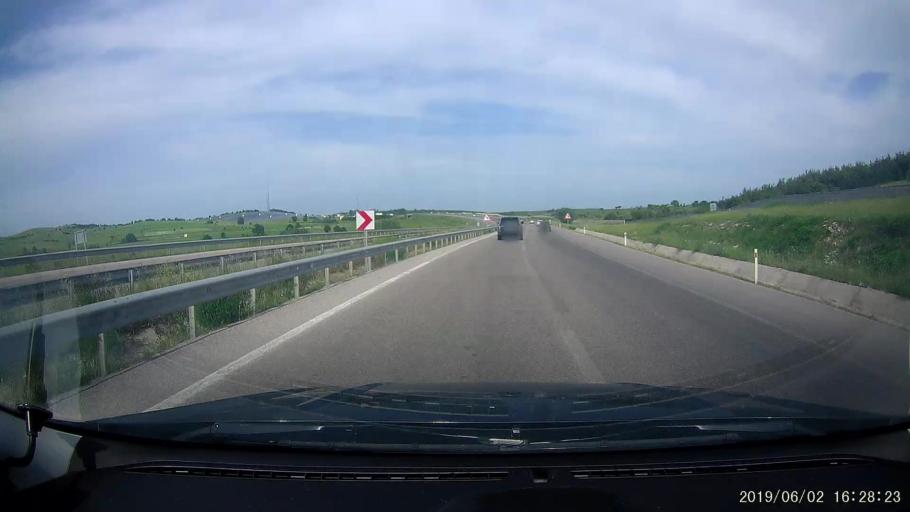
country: TR
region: Samsun
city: Ladik
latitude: 41.0068
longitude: 35.8462
